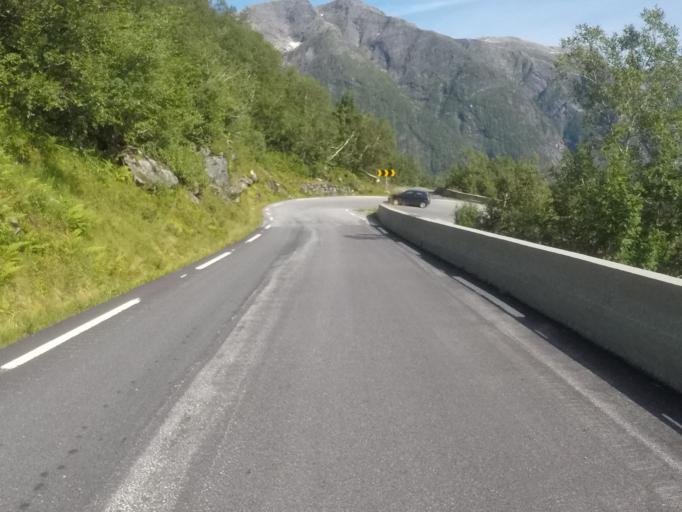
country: NO
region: Sogn og Fjordane
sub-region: Balestrand
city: Balestrand
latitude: 61.3575
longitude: 6.5225
